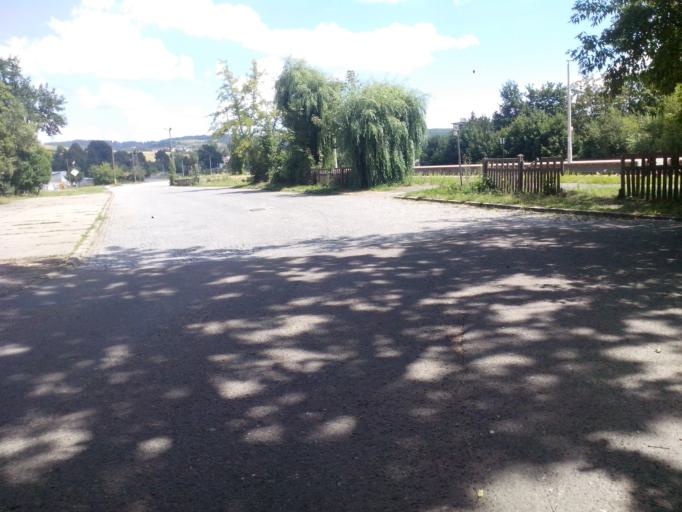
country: PL
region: Subcarpathian Voivodeship
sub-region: Powiat strzyzowski
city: Strzyzow
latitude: 49.8696
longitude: 21.8013
